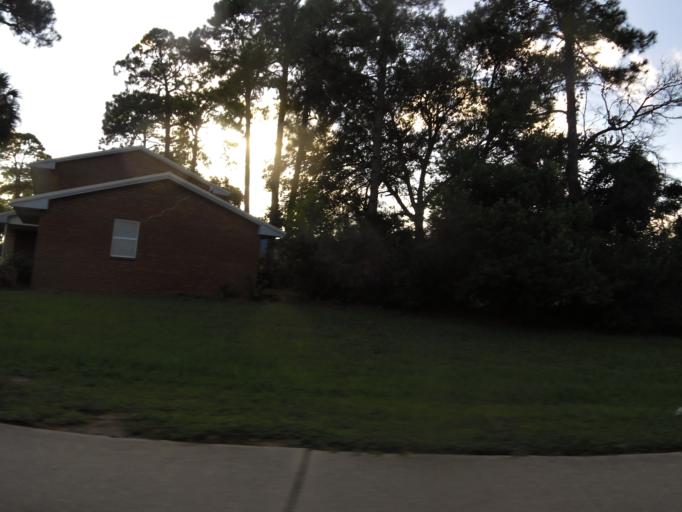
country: US
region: Georgia
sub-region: Glynn County
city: Brunswick
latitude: 31.1709
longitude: -81.4921
